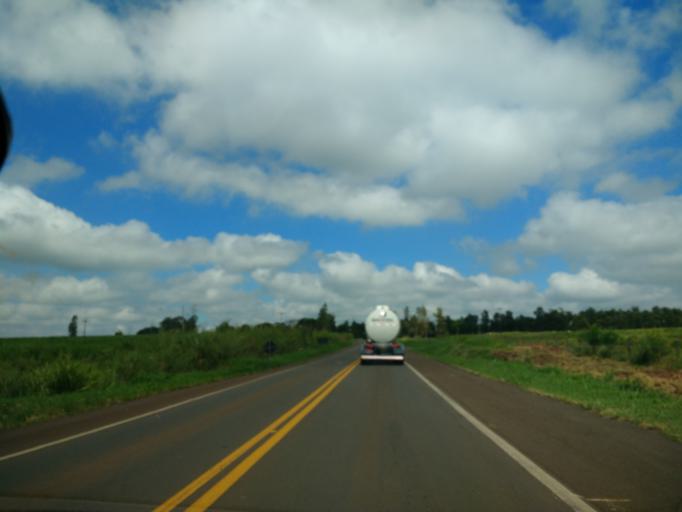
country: BR
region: Parana
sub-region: Cruzeiro Do Oeste
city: Cruzeiro do Oeste
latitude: -23.7775
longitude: -53.0246
